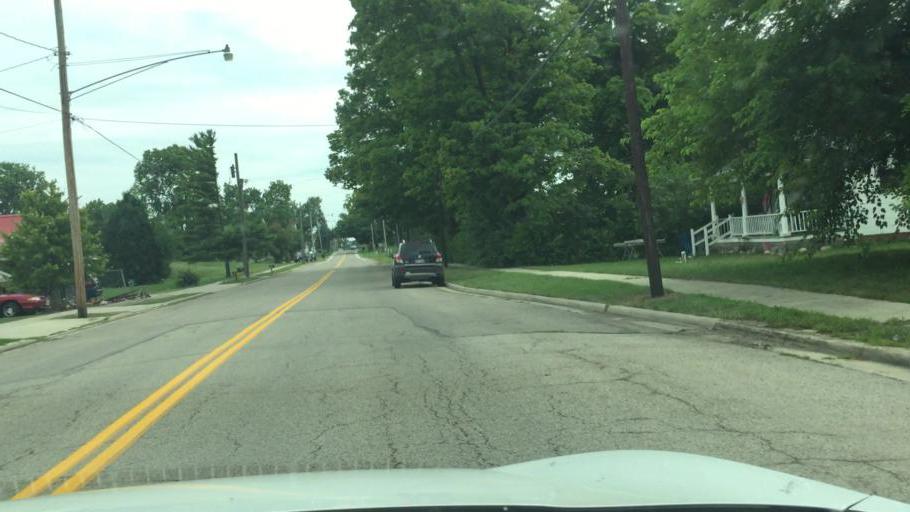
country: US
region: Ohio
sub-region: Champaign County
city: North Lewisburg
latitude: 40.1733
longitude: -83.5275
